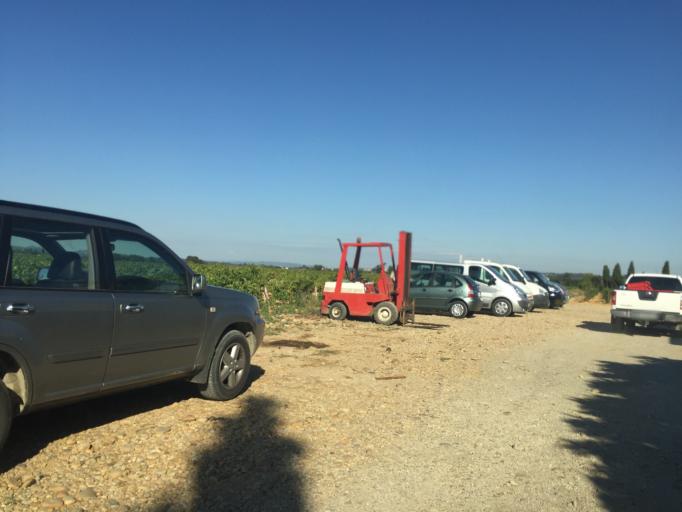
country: FR
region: Provence-Alpes-Cote d'Azur
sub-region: Departement du Vaucluse
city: Sorgues
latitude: 44.0323
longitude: 4.8581
